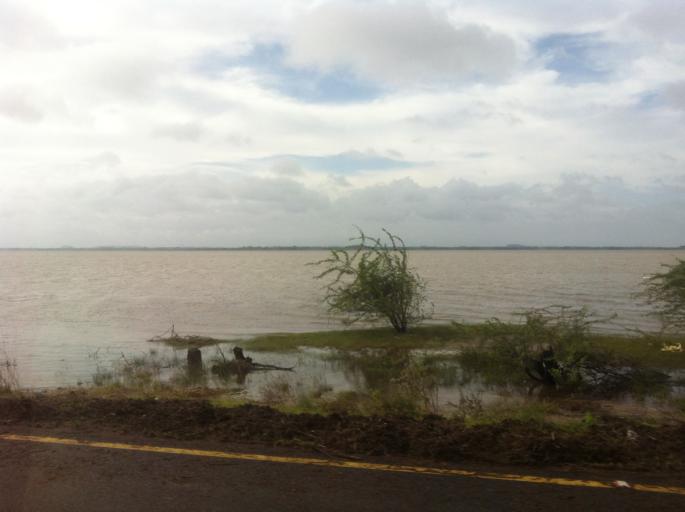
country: IN
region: Tamil Nadu
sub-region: Kancheepuram
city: Cheyyur
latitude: 12.3458
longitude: 80.0525
